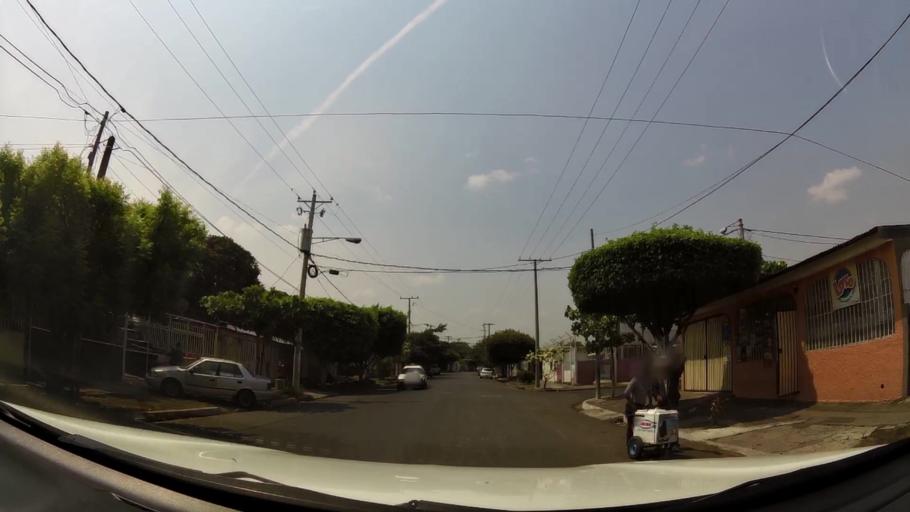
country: NI
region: Managua
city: Ciudad Sandino
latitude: 12.1555
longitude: -86.3128
